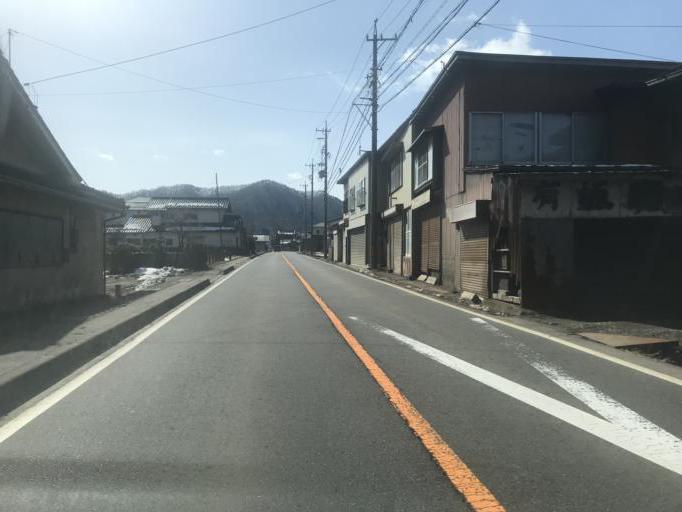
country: JP
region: Nagano
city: Saku
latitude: 36.0249
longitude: 138.4887
